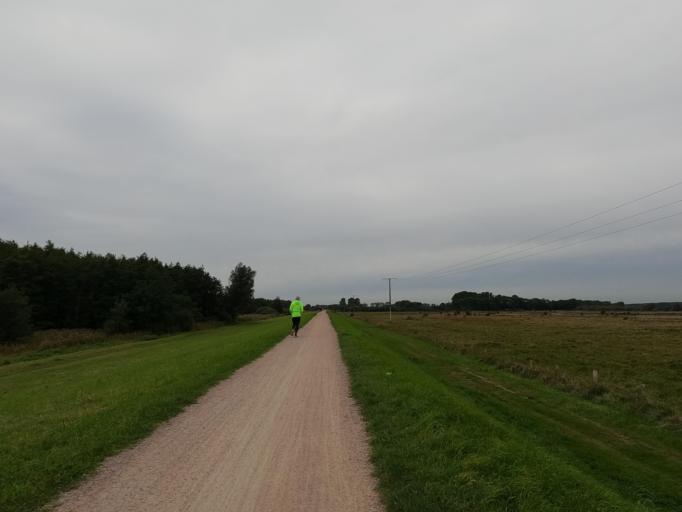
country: DE
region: Schleswig-Holstein
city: Kellenhusen
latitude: 54.1772
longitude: 11.0437
